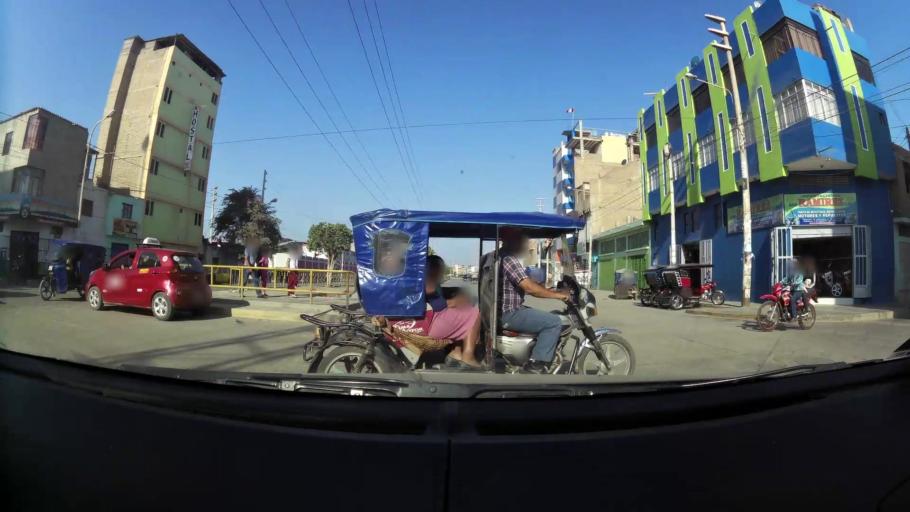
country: PE
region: Lambayeque
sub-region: Provincia de Chiclayo
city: Santa Rosa
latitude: -6.7630
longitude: -79.8366
